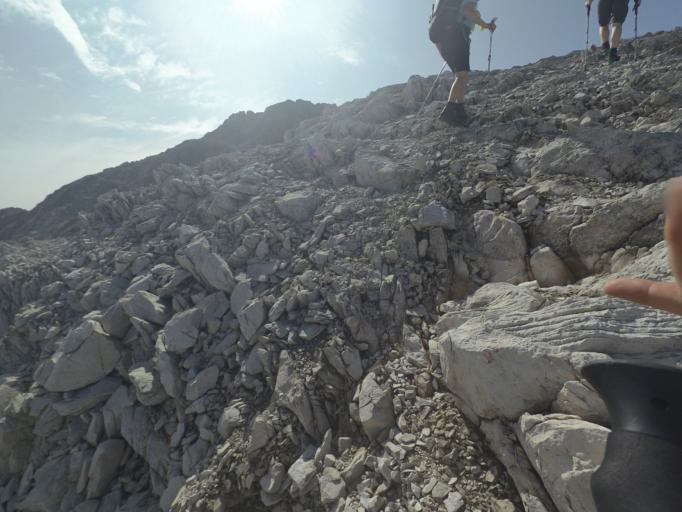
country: AT
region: Salzburg
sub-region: Politischer Bezirk Sankt Johann im Pongau
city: Kleinarl
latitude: 47.2101
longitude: 13.3999
